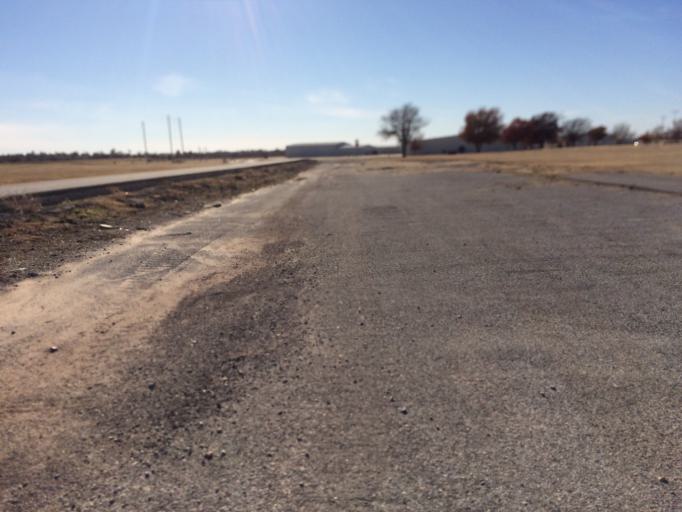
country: US
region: Oklahoma
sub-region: Cleveland County
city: Norman
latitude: 35.2418
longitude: -97.4641
